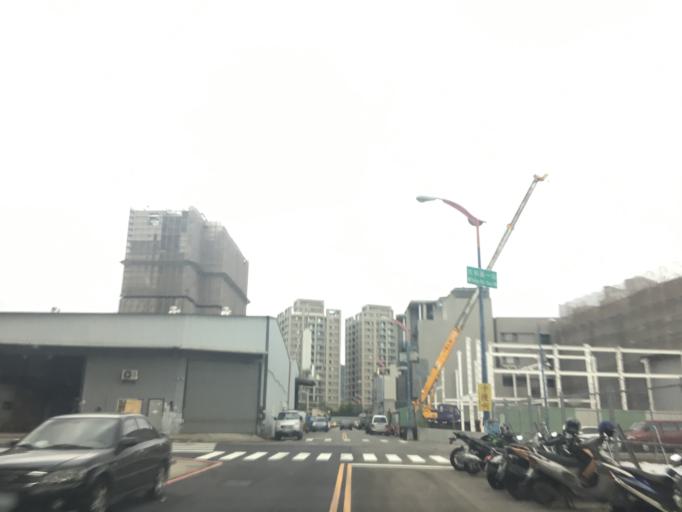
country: TW
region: Taiwan
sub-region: Taichung City
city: Taichung
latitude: 24.1609
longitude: 120.7245
